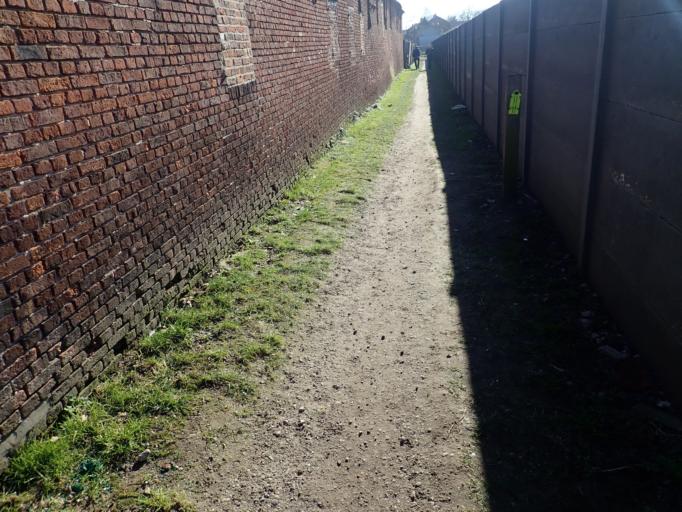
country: BE
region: Flanders
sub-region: Provincie Oost-Vlaanderen
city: Hamme
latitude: 51.0666
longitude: 4.1542
